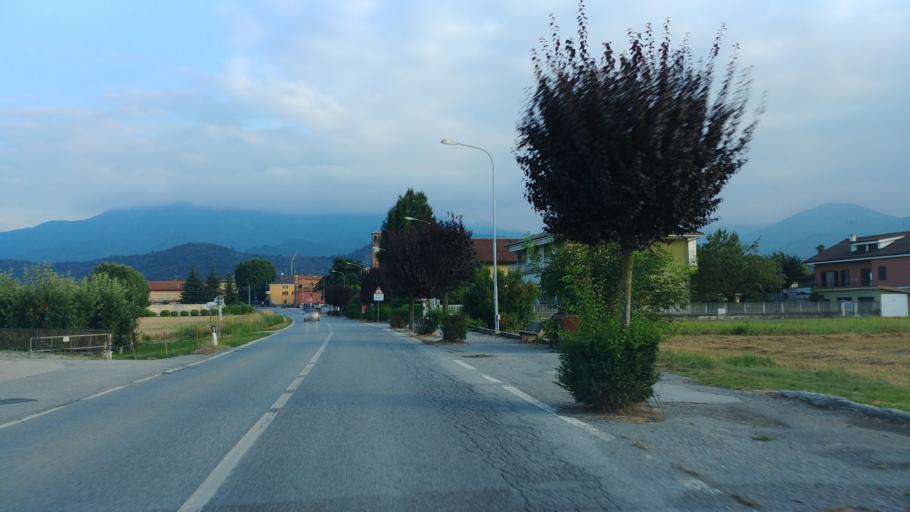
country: IT
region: Piedmont
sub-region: Provincia di Cuneo
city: Peveragno
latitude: 44.3496
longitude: 7.5930
